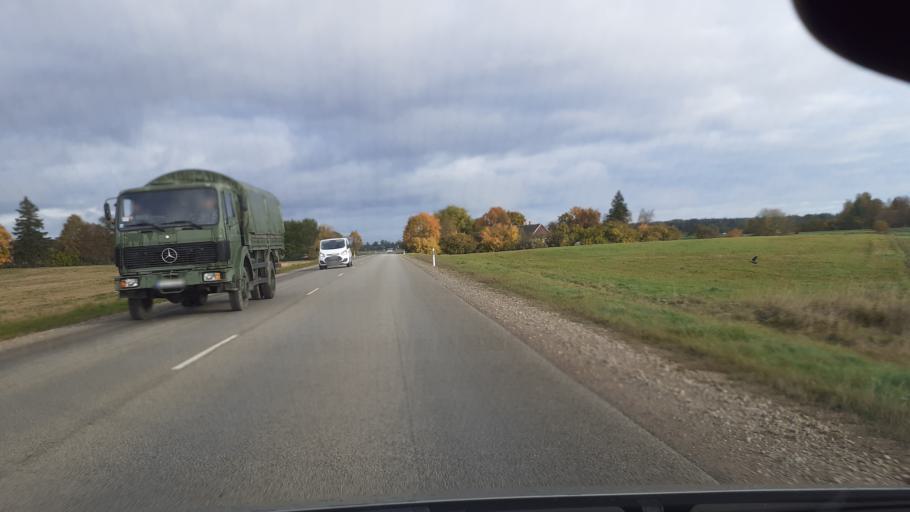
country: LV
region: Kuldigas Rajons
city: Kuldiga
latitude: 56.9803
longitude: 21.9314
